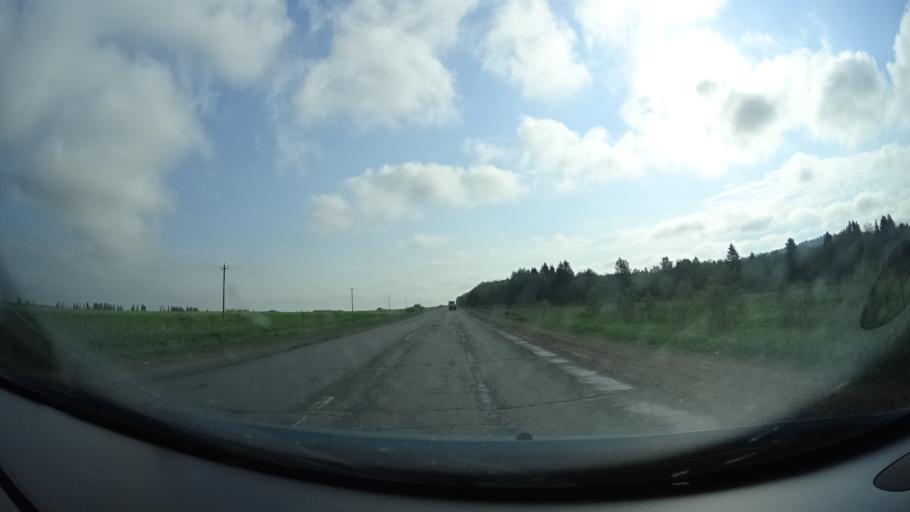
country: RU
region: Perm
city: Kultayevo
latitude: 57.8545
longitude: 55.8547
